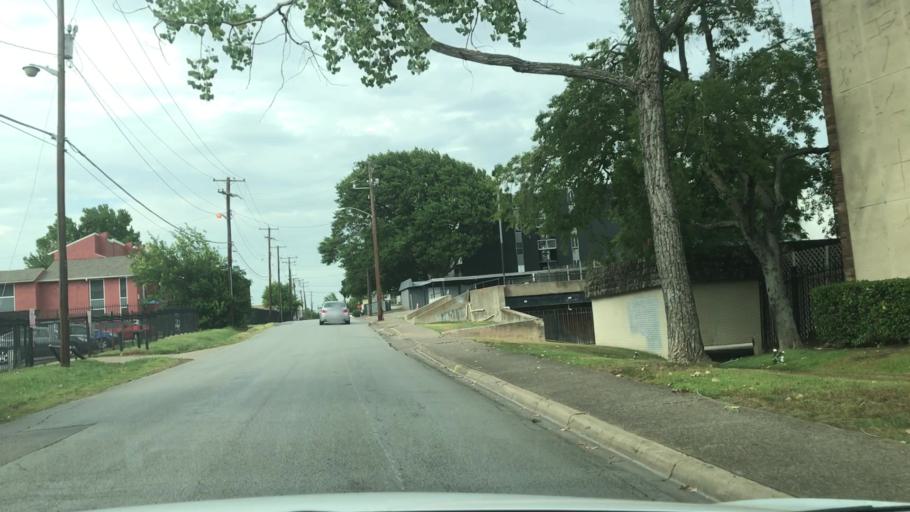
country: US
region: Texas
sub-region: Dallas County
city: University Park
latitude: 32.8690
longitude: -96.7607
